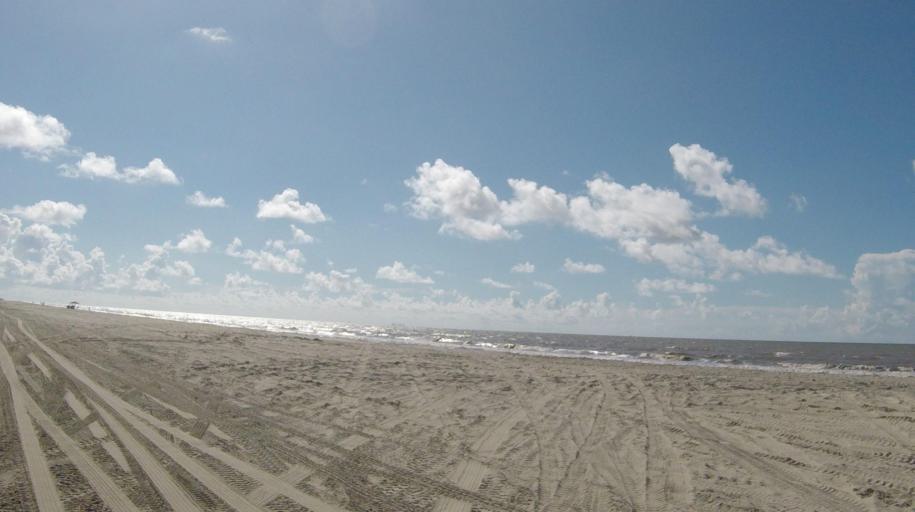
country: US
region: Louisiana
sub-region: Cameron Parish
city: Cameron
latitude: 29.7694
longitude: -93.4541
